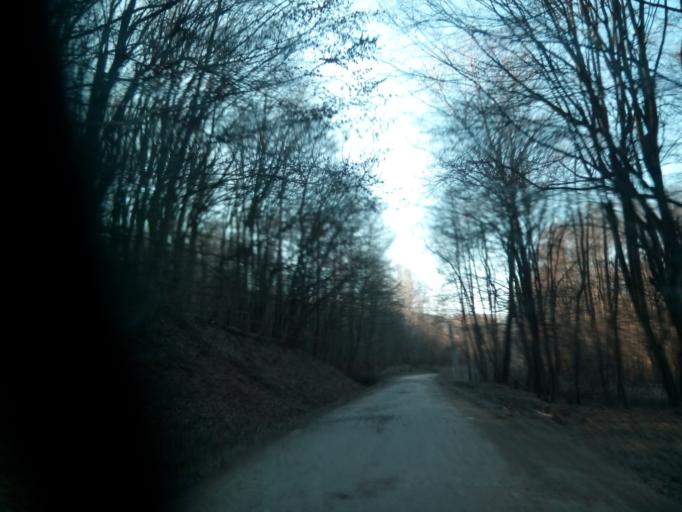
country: SK
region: Kosicky
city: Medzev
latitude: 48.6860
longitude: 20.9066
